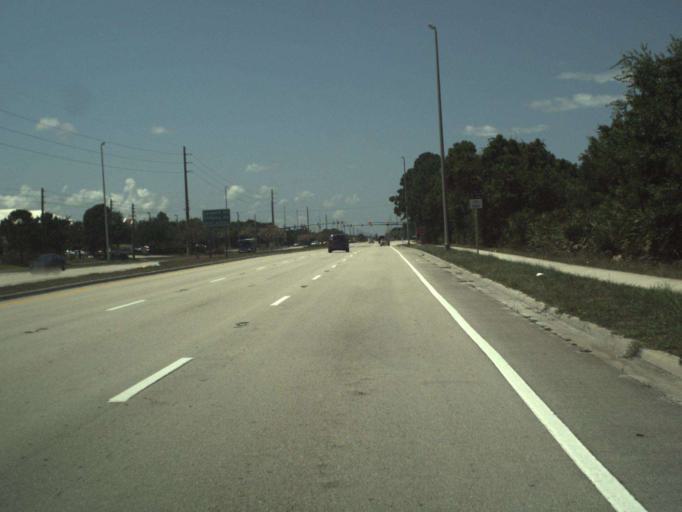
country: US
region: Florida
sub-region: Saint Lucie County
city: Port Saint Lucie
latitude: 27.2843
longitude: -80.2959
